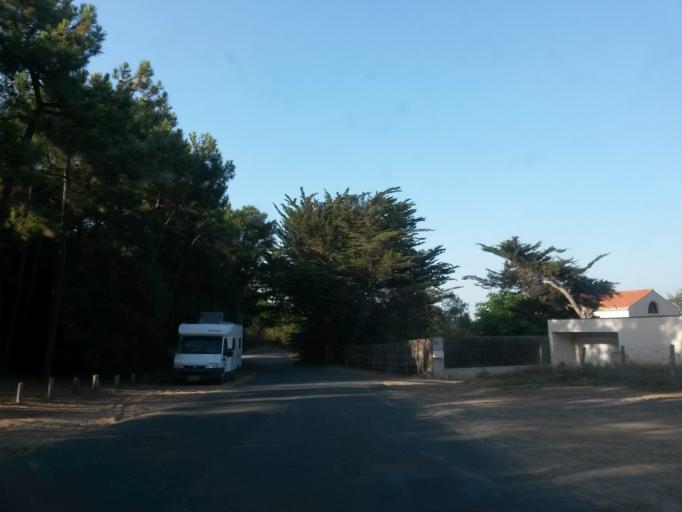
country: FR
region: Pays de la Loire
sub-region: Departement de la Vendee
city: Les Sables-d'Olonne
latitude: 46.5128
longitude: -1.8074
